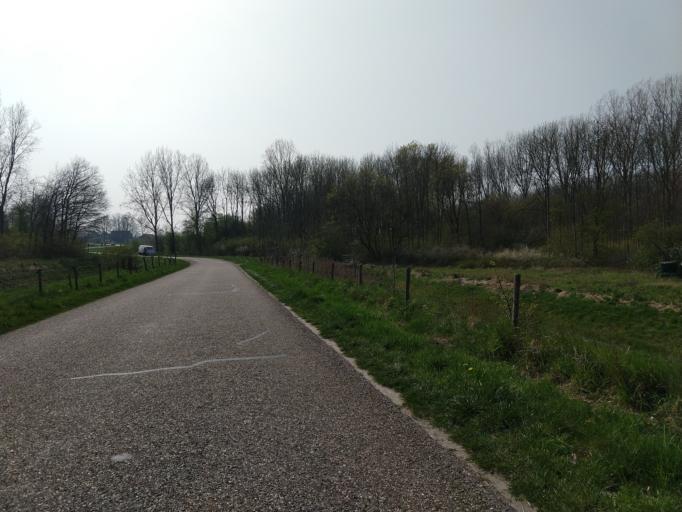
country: NL
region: Zeeland
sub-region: Gemeente Reimerswaal
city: Yerseke
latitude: 51.5224
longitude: 3.9856
